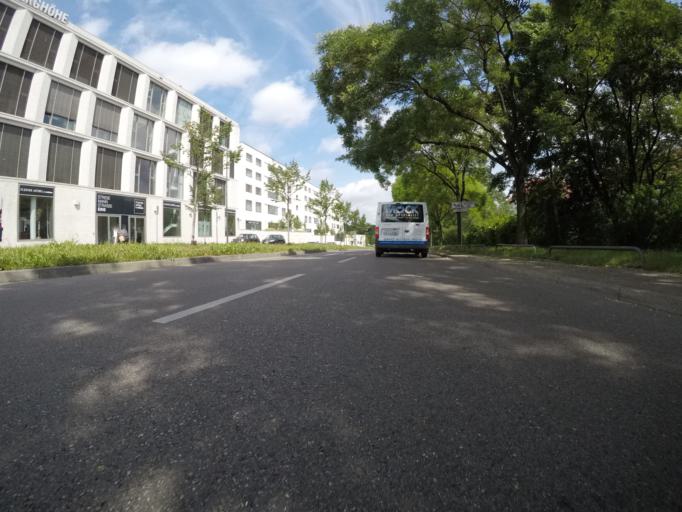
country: DE
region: Baden-Wuerttemberg
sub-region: Regierungsbezirk Stuttgart
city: Stuttgart
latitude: 48.7998
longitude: 9.1734
